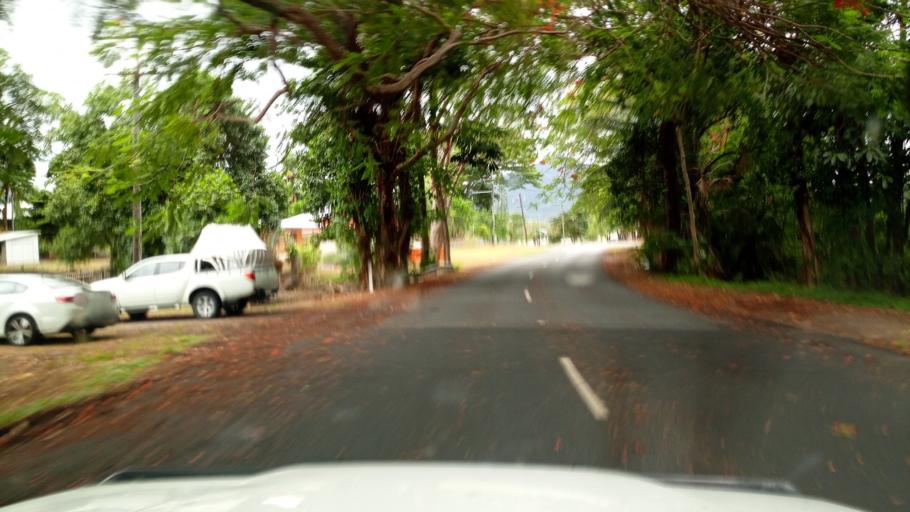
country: AU
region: Queensland
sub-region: Cairns
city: Redlynch
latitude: -16.8830
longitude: 145.7131
